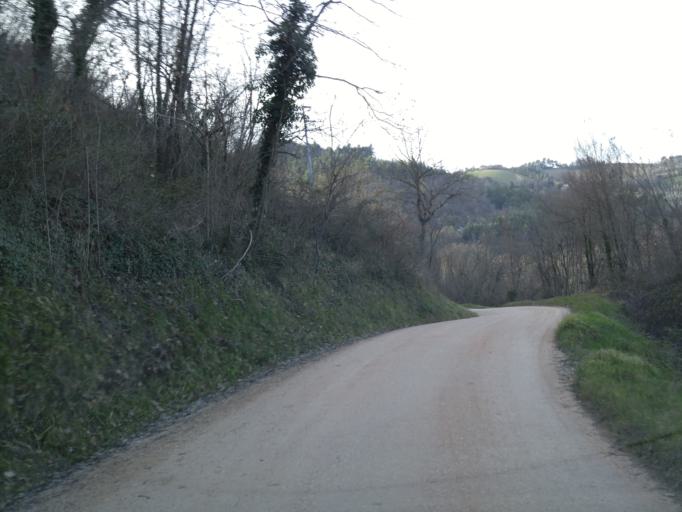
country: IT
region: The Marches
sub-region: Provincia di Pesaro e Urbino
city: Canavaccio
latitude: 43.6966
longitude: 12.6821
